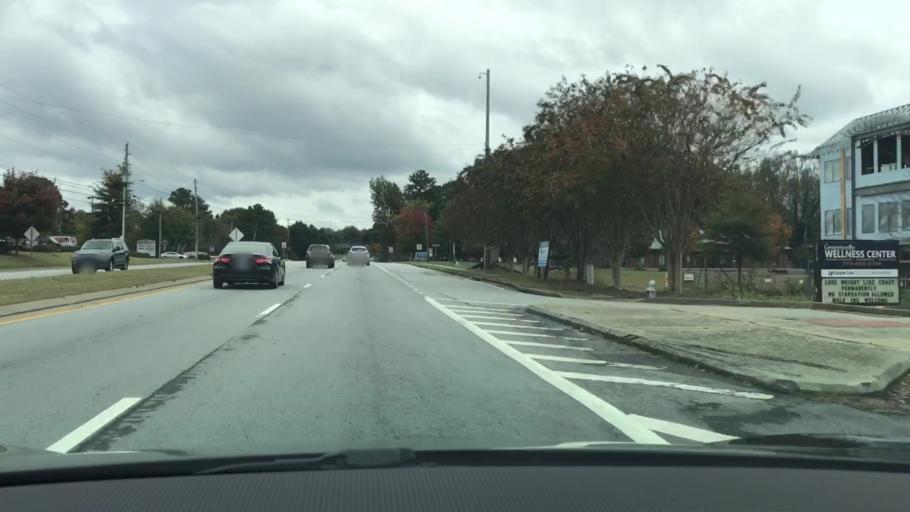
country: US
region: Georgia
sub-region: Gwinnett County
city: Suwanee
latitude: 33.9999
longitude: -84.0383
